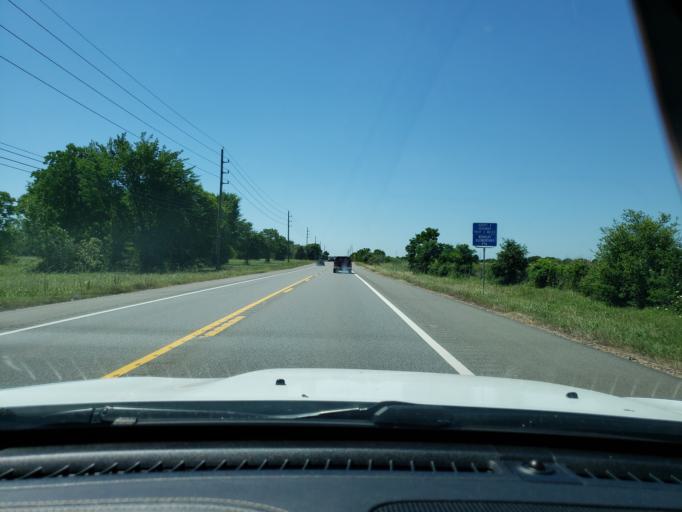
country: US
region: Texas
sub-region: Fort Bend County
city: Fulshear
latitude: 29.6915
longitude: -95.8460
